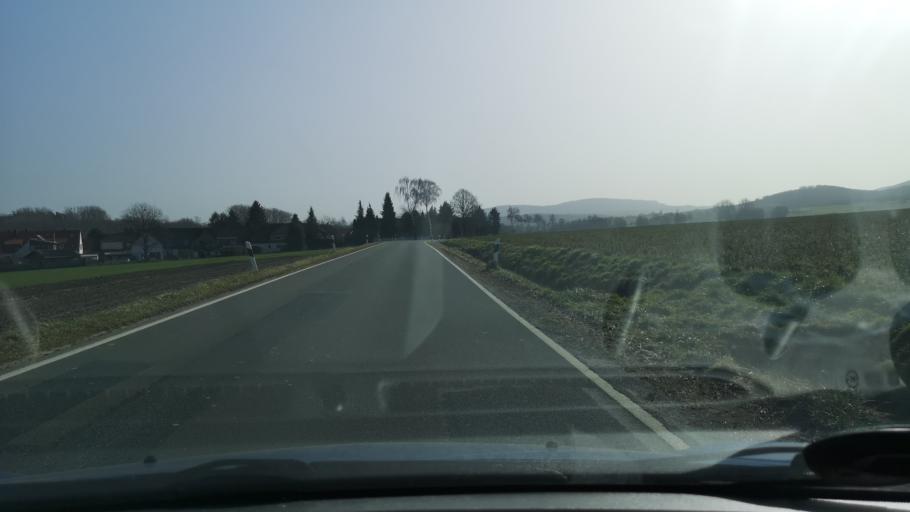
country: DE
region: Lower Saxony
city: Weenzen
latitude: 52.0142
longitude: 9.6283
